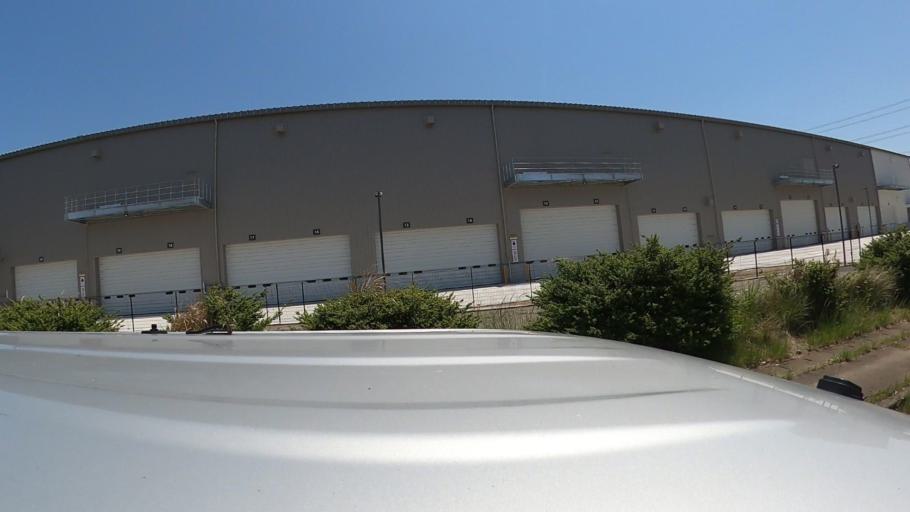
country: JP
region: Ibaraki
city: Ushiku
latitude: 36.0186
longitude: 140.0848
